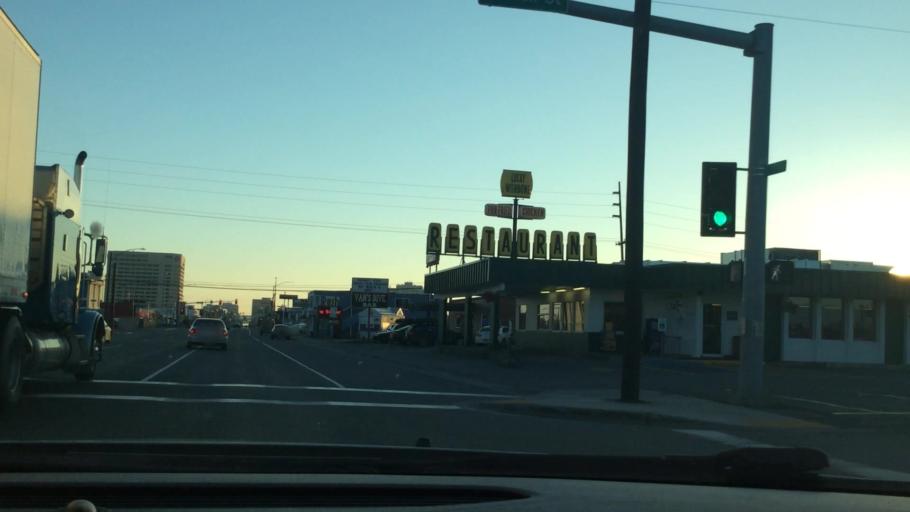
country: US
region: Alaska
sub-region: Anchorage Municipality
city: Anchorage
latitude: 61.2176
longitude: -149.8627
